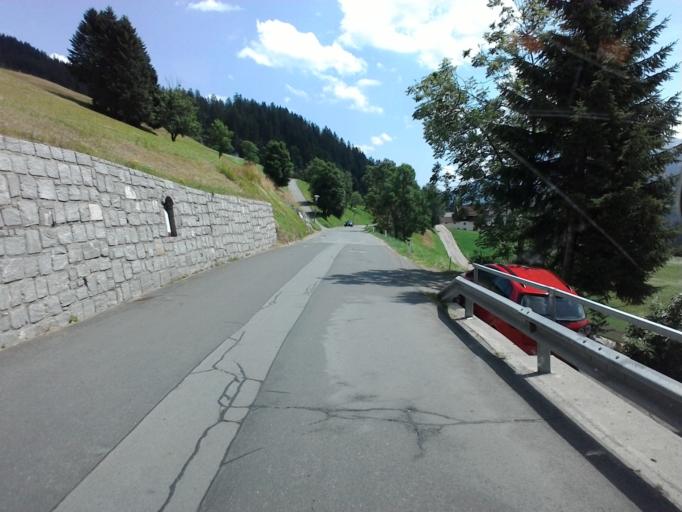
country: AT
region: Tyrol
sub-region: Politischer Bezirk Lienz
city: Untertilliach
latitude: 46.7018
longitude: 12.7865
